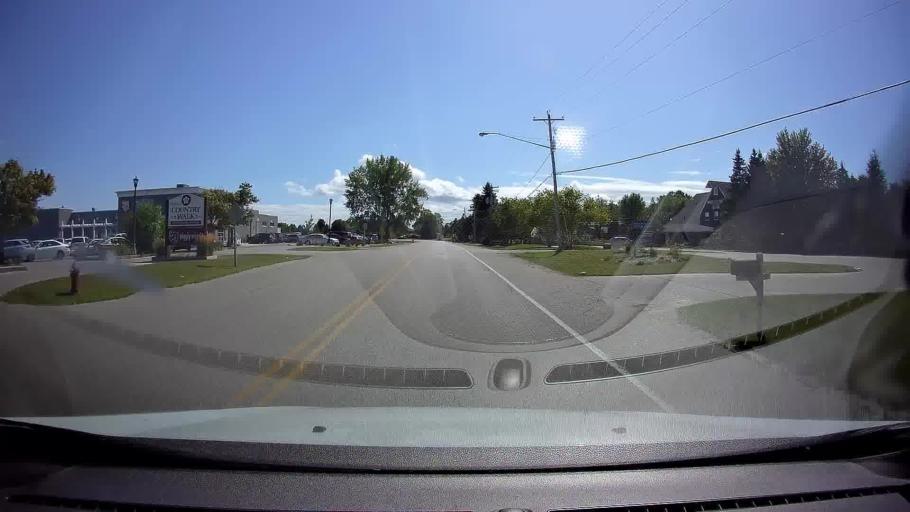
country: US
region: Wisconsin
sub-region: Door County
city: Sturgeon Bay
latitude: 45.1849
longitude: -87.1274
